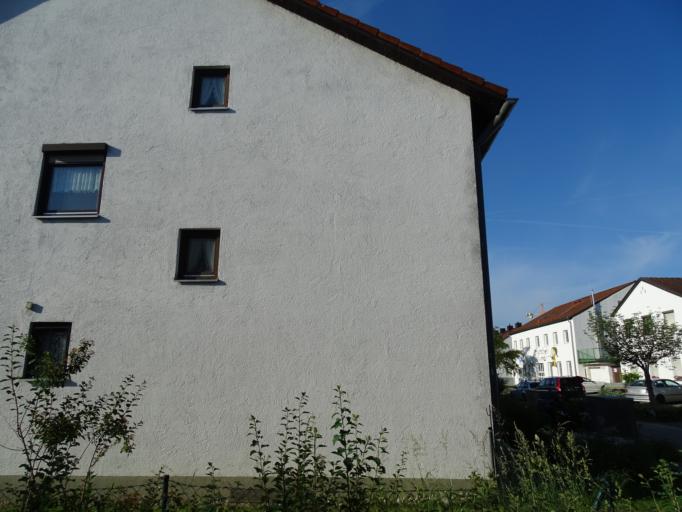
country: DE
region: Bavaria
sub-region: Upper Bavaria
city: Oberschleissheim
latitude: 48.2052
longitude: 11.5799
